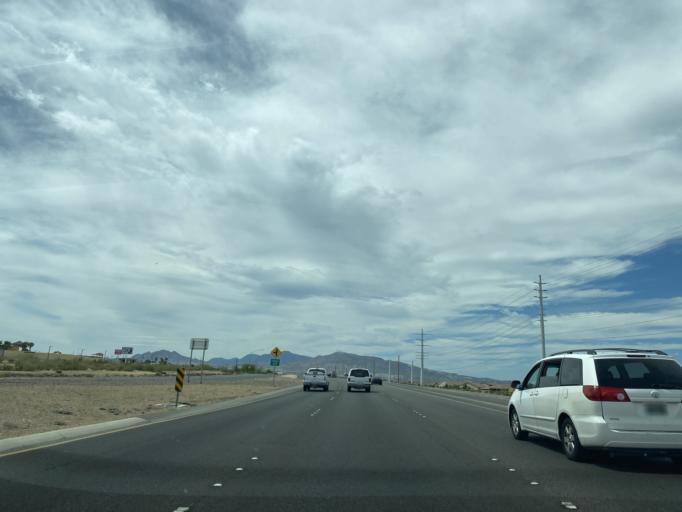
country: US
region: Nevada
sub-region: Clark County
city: Henderson
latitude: 36.0713
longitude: -114.9570
